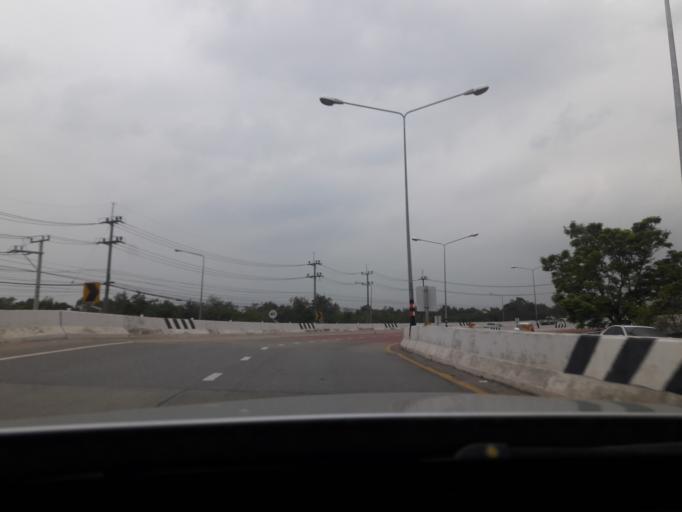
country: TH
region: Samut Songkhram
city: Samut Songkhram
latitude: 13.3994
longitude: 100.0093
